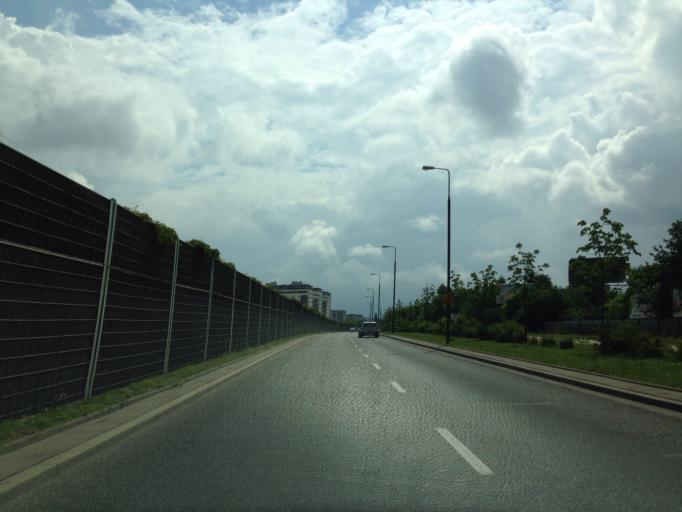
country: PL
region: Masovian Voivodeship
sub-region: Warszawa
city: Bielany
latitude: 52.2678
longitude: 20.9370
